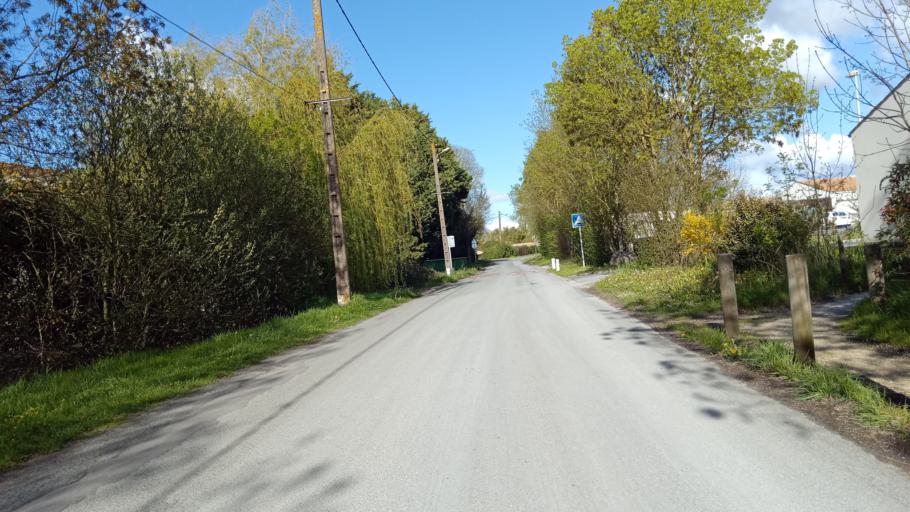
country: FR
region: Poitou-Charentes
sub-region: Departement de la Charente-Maritime
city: Verines
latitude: 46.1470
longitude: -0.9448
